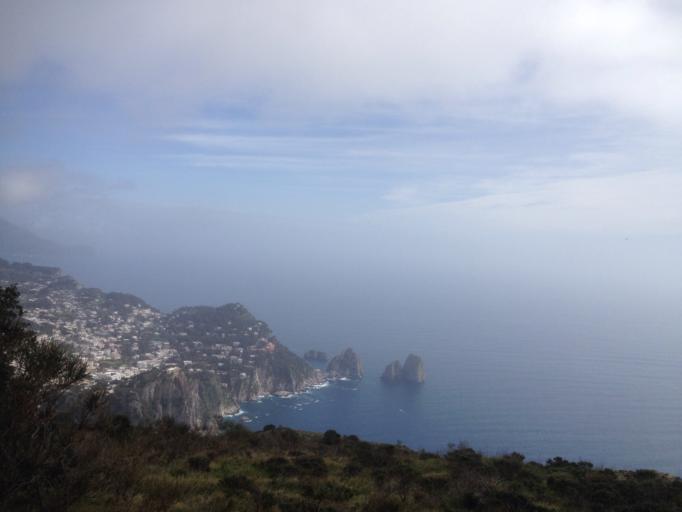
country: IT
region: Campania
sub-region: Provincia di Napoli
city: Anacapri
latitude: 40.5452
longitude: 14.2240
